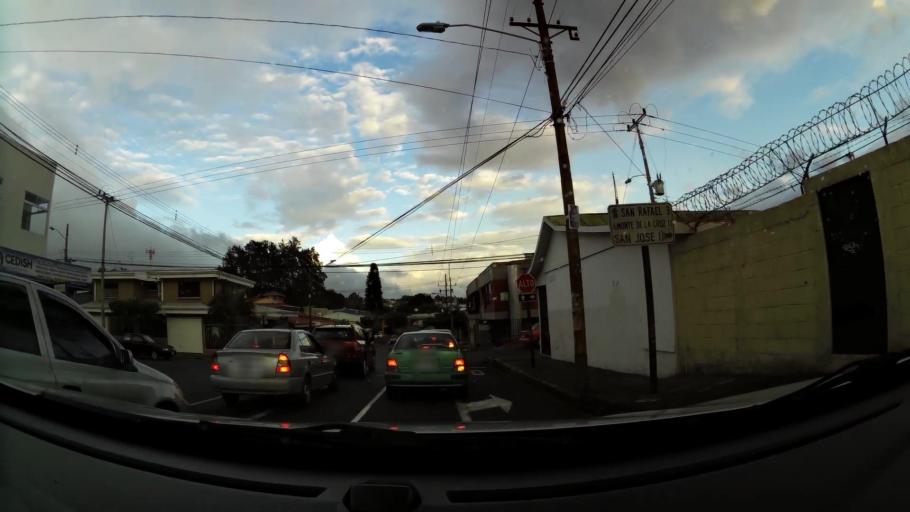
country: CR
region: Heredia
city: Heredia
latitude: 10.0027
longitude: -84.1136
